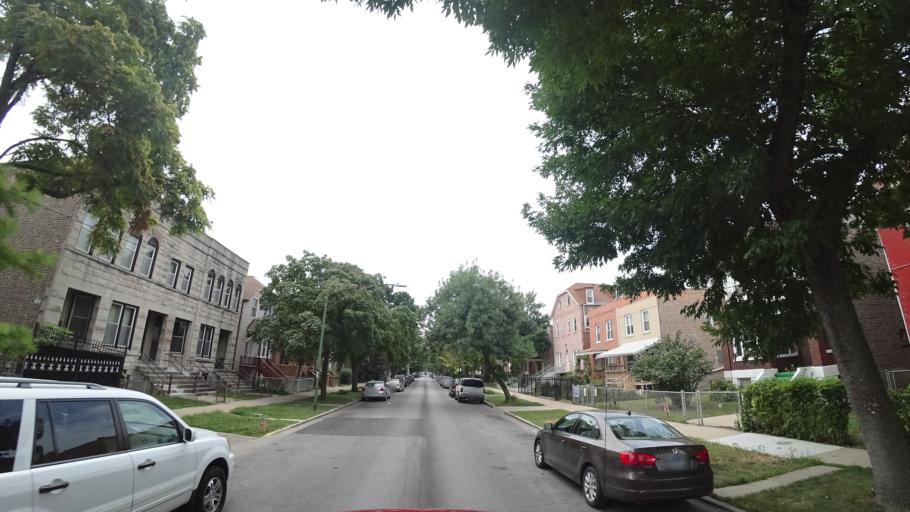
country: US
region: Illinois
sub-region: Cook County
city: Cicero
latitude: 41.8491
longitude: -87.7174
